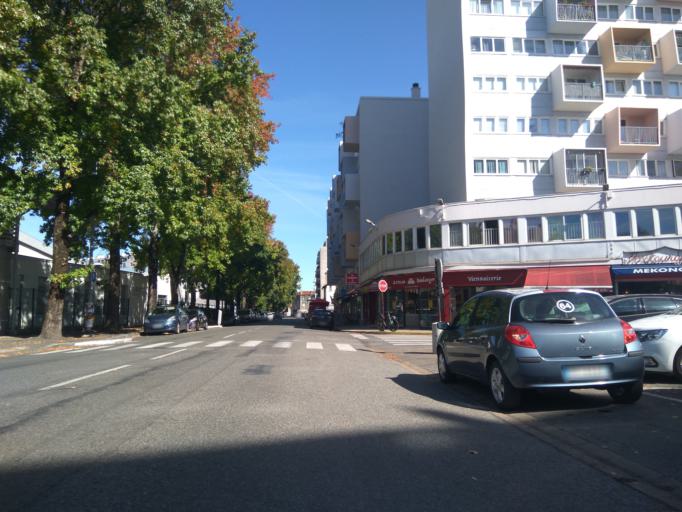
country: FR
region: Aquitaine
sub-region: Departement des Pyrenees-Atlantiques
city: Pau
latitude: 43.3033
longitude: -0.3784
